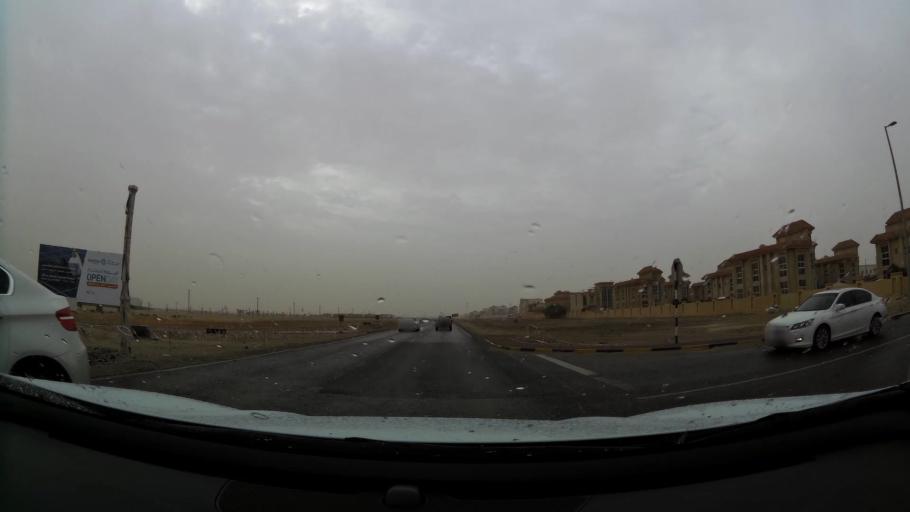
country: AE
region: Abu Dhabi
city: Abu Dhabi
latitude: 24.4355
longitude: 54.6032
